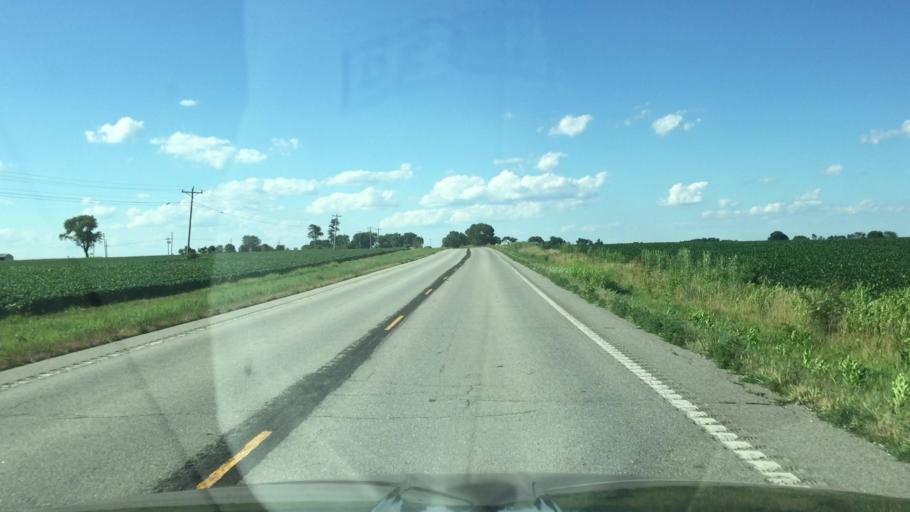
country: US
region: Missouri
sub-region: Moniteau County
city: Tipton
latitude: 38.6003
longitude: -92.7894
